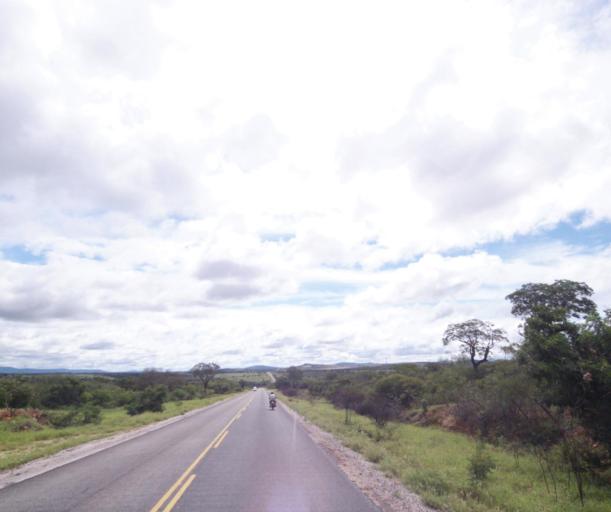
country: BR
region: Bahia
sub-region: Brumado
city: Brumado
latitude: -14.1511
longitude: -41.5063
